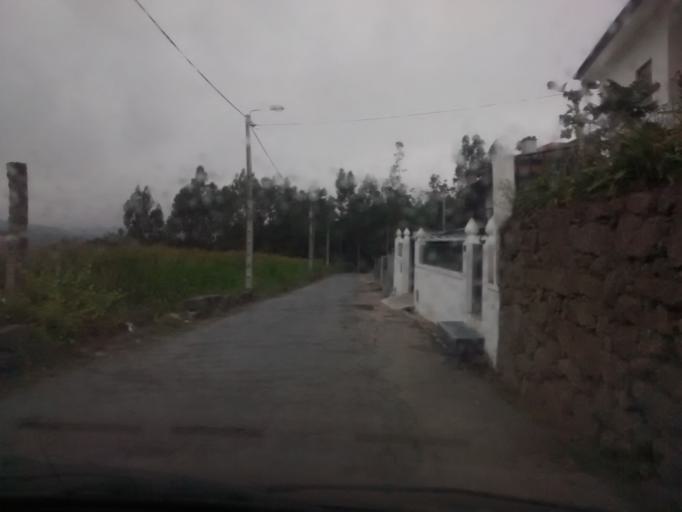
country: PT
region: Braga
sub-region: Vila Nova de Famalicao
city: Vila Nova de Famalicao
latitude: 41.4569
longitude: -8.5242
